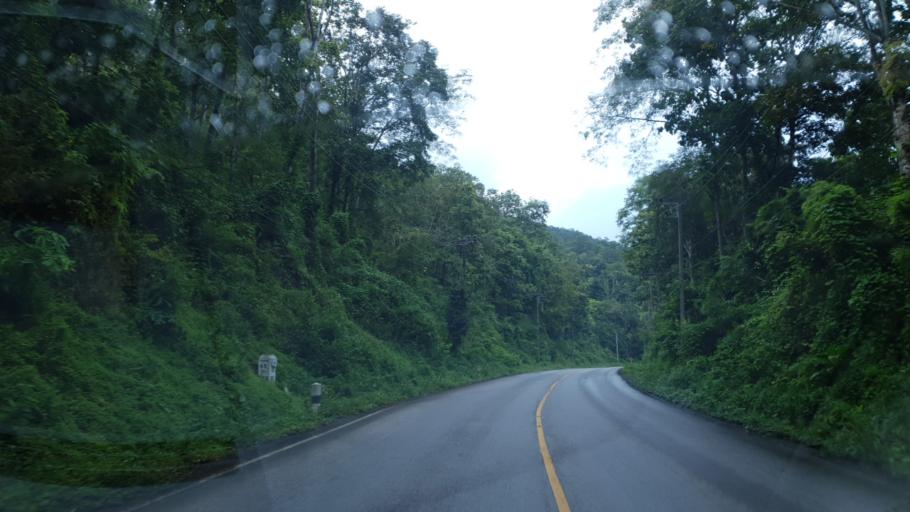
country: TH
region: Mae Hong Son
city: Ban Huai I Huak
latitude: 18.1575
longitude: 97.9662
